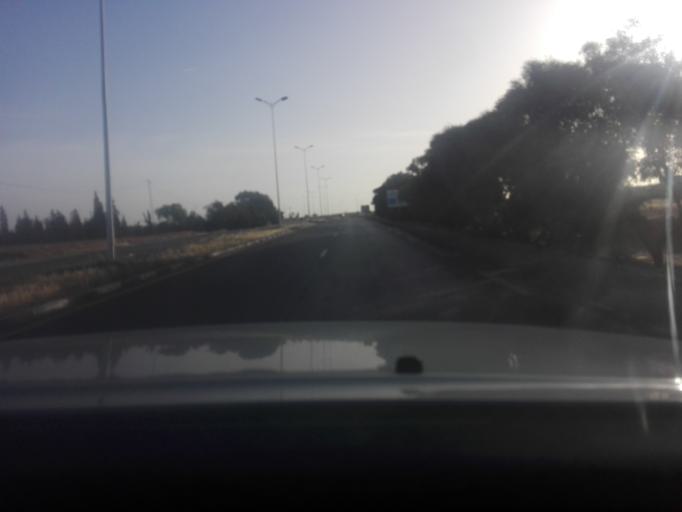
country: TN
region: Safaqis
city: Al Qarmadah
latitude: 34.8543
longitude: 10.7575
